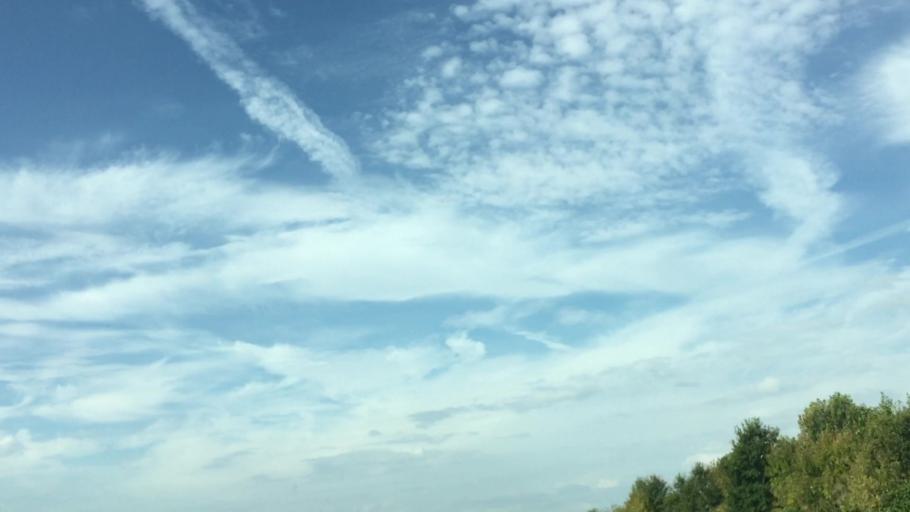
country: US
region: Illinois
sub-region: Rock Island County
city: Port Byron
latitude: 41.5432
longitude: -90.2636
